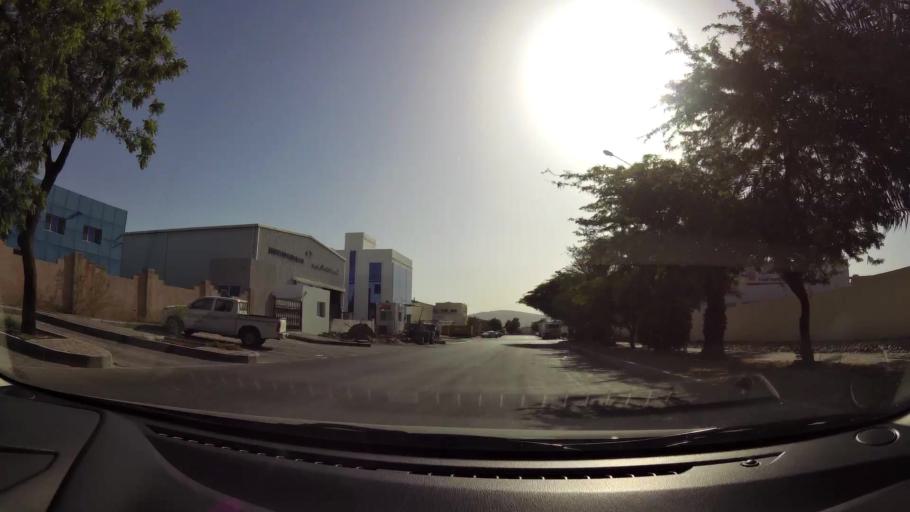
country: OM
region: Muhafazat Masqat
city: As Sib al Jadidah
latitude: 23.5535
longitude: 58.2220
